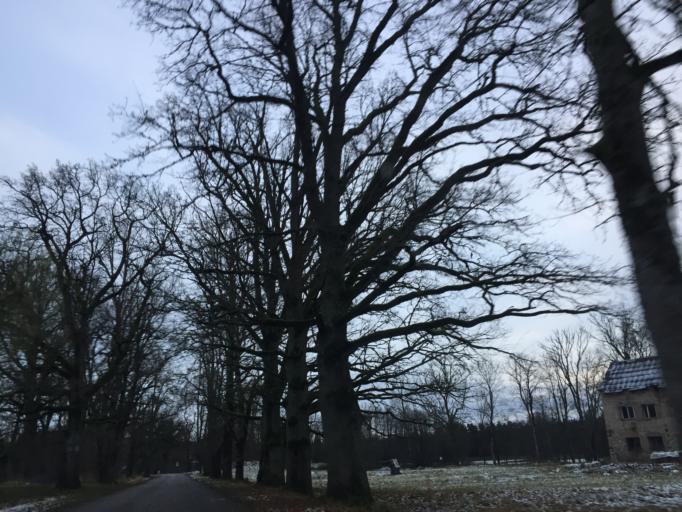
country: LV
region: Burtnieki
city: Matisi
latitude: 57.6396
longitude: 25.0406
